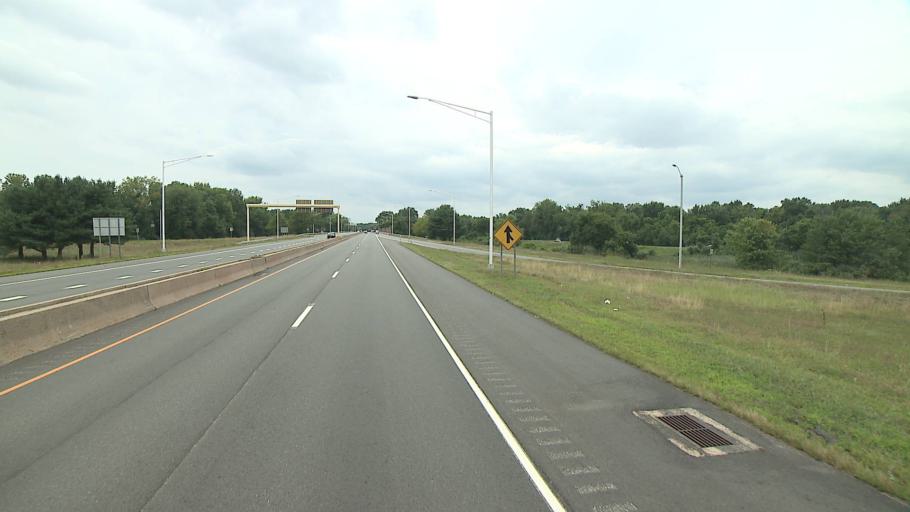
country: US
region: Connecticut
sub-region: Hartford County
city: Glastonbury
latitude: 41.7241
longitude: -72.6210
